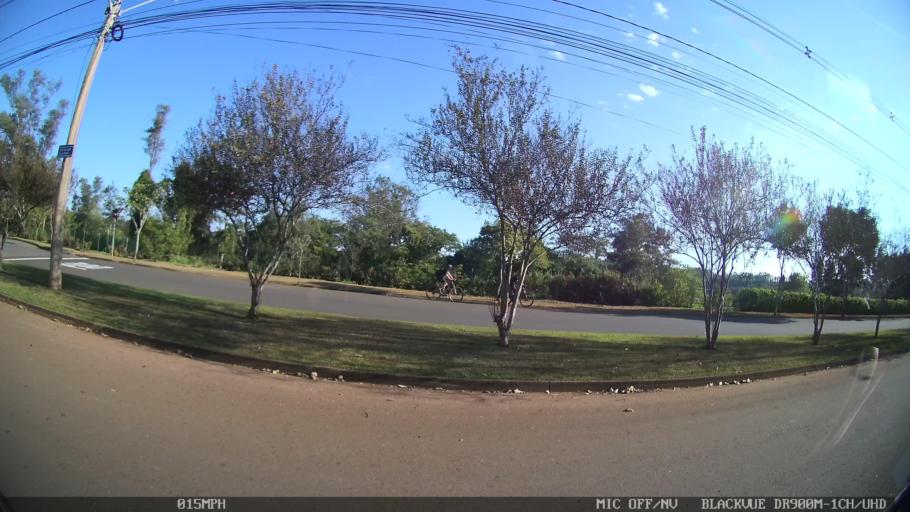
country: BR
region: Sao Paulo
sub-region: Piracicaba
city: Piracicaba
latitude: -22.6905
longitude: -47.6292
